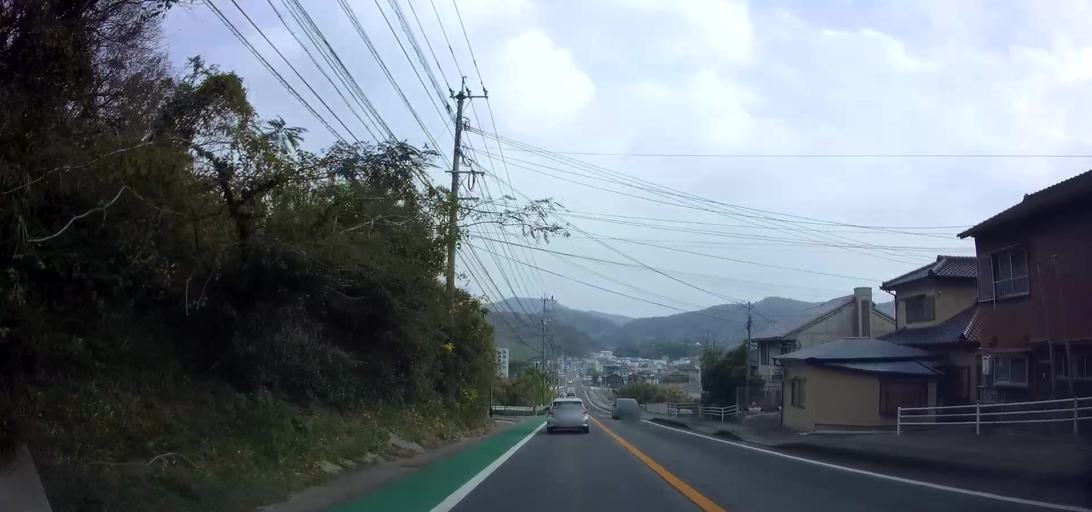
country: JP
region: Nagasaki
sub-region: Isahaya-shi
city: Isahaya
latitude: 32.7948
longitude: 130.0782
